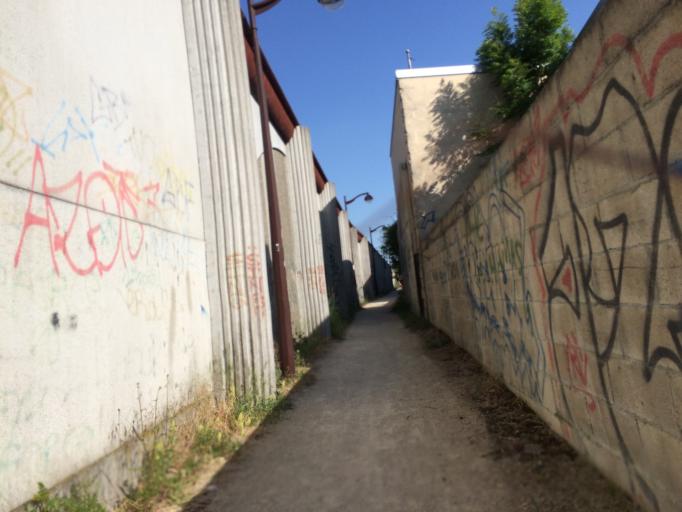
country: FR
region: Ile-de-France
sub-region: Departement de l'Essonne
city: Morsang-sur-Orge
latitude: 48.6603
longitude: 2.3714
